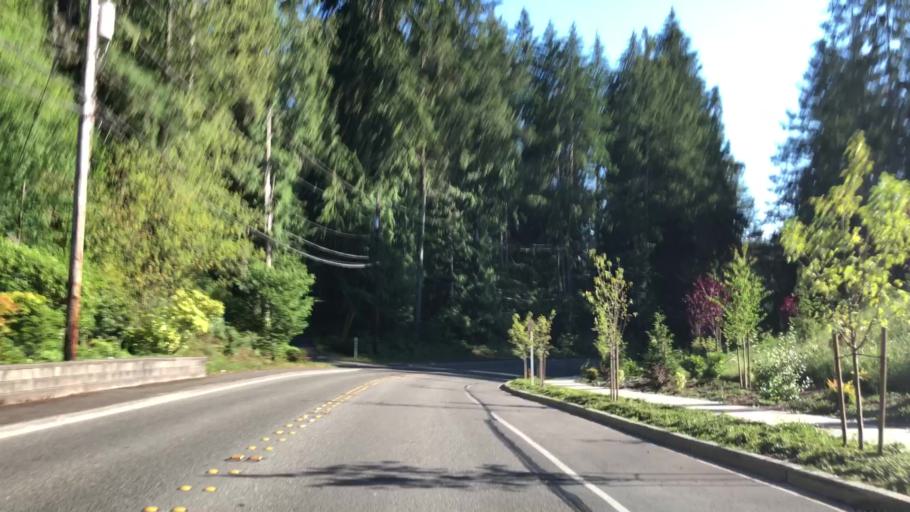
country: US
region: Washington
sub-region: Snohomish County
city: Martha Lake
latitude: 47.8307
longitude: -122.2519
